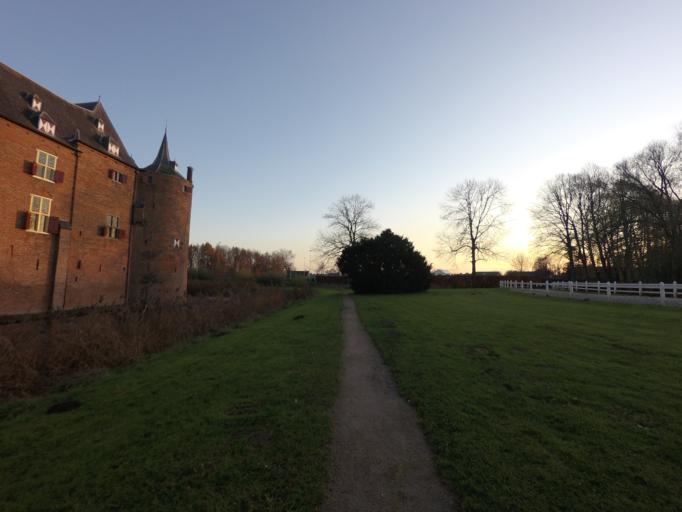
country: NL
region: Gelderland
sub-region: Gemeente Maasdriel
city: Hedel
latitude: 51.7517
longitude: 5.2288
